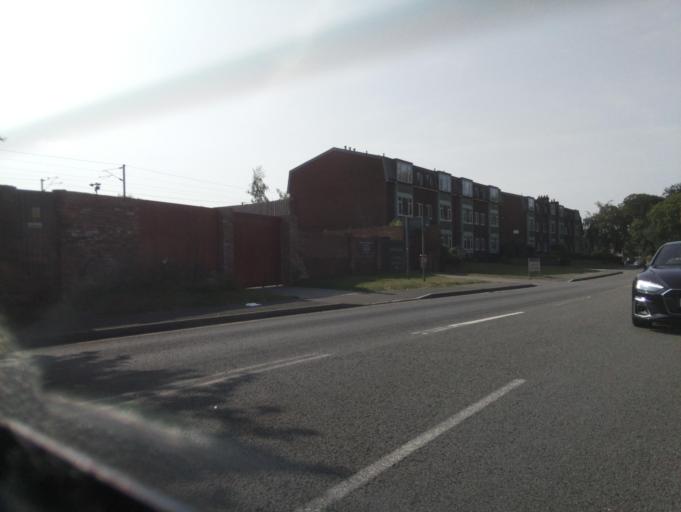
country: GB
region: England
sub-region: Staffordshire
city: Lichfield
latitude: 52.6797
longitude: -1.8275
